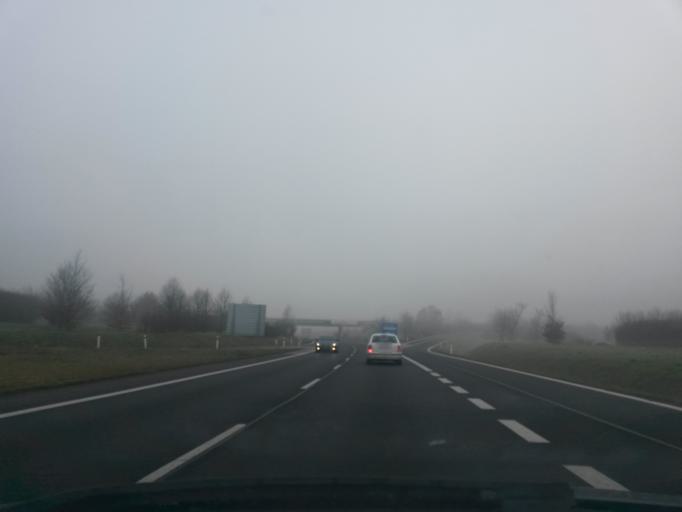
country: CZ
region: Ustecky
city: Cerncice
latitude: 50.3385
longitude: 13.8305
